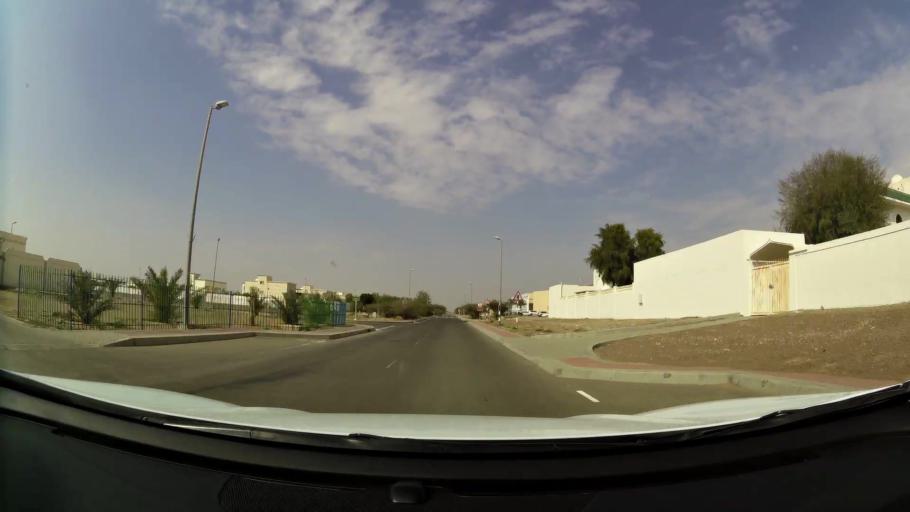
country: AE
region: Abu Dhabi
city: Al Ain
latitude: 24.0980
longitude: 55.9049
